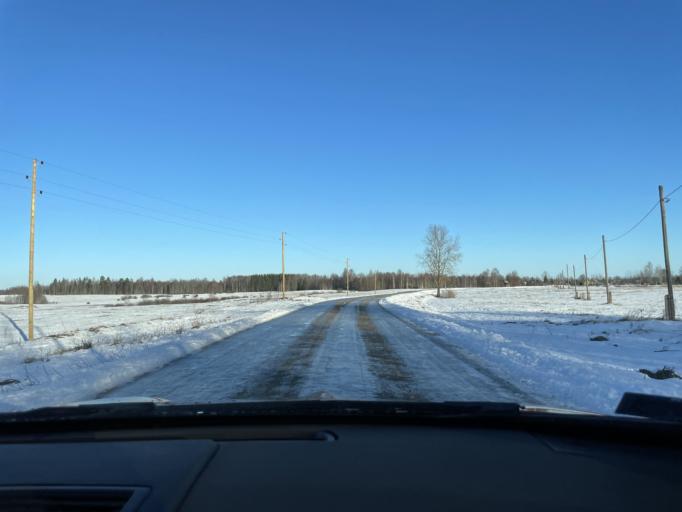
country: LV
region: Ludzas Rajons
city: Ludza
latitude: 56.4608
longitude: 27.5701
